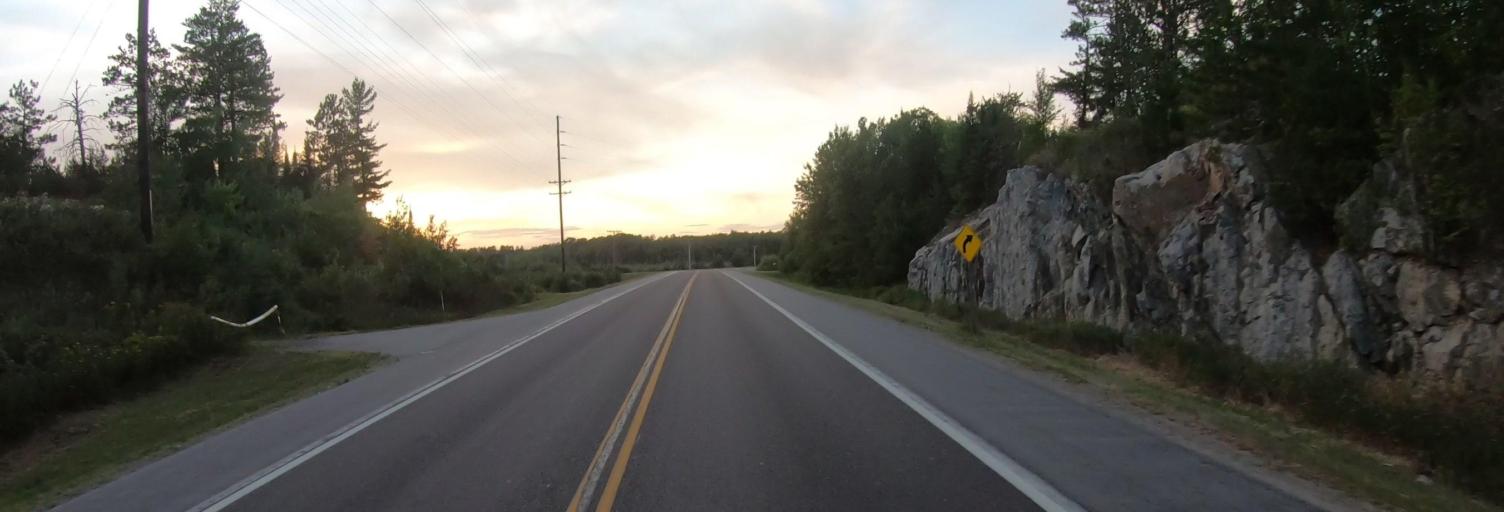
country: US
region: Minnesota
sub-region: Saint Louis County
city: Aurora
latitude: 47.7946
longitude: -92.3712
